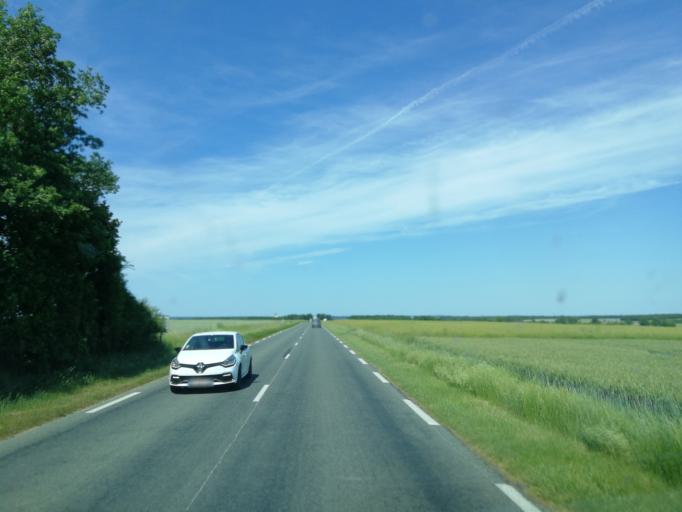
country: FR
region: Poitou-Charentes
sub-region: Departement de la Vienne
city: Loudun
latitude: 47.0450
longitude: 0.1349
